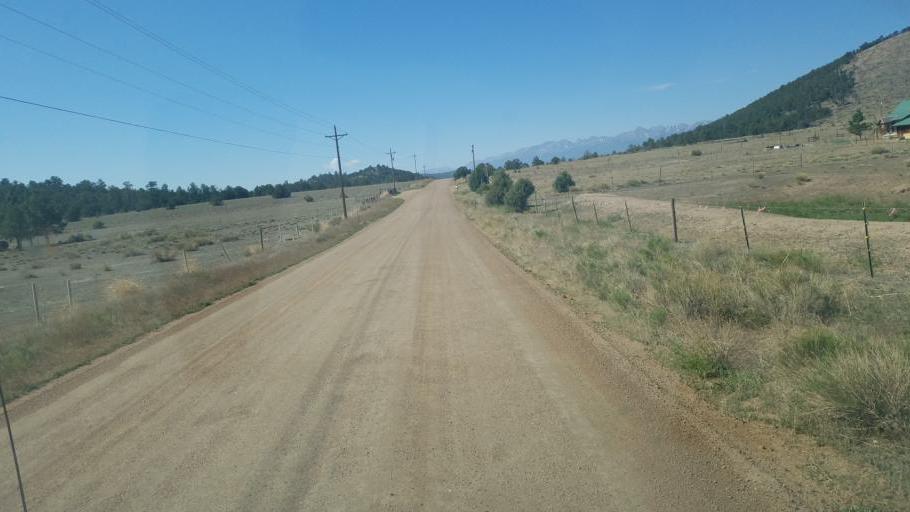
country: US
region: Colorado
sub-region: Custer County
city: Westcliffe
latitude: 38.3080
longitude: -105.4864
